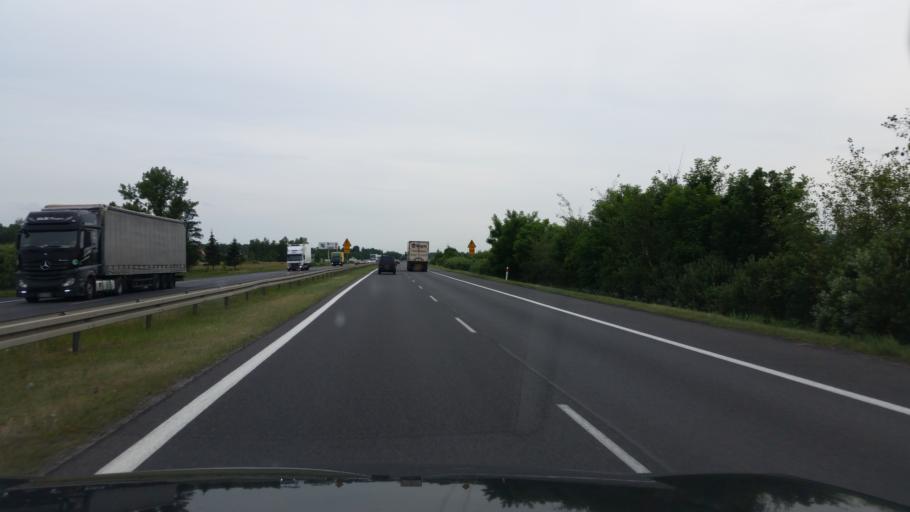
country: PL
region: Lodz Voivodeship
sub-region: Powiat radomszczanski
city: Kamiensk
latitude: 51.2387
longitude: 19.5191
